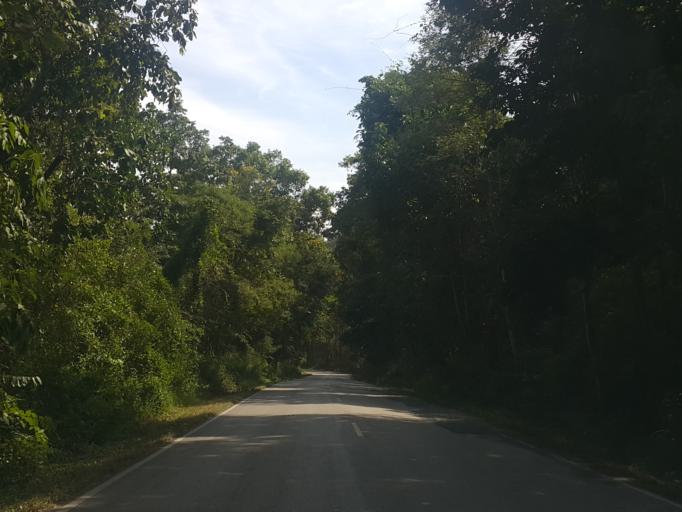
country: TH
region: Chiang Mai
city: Mae On
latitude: 18.8305
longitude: 99.1976
